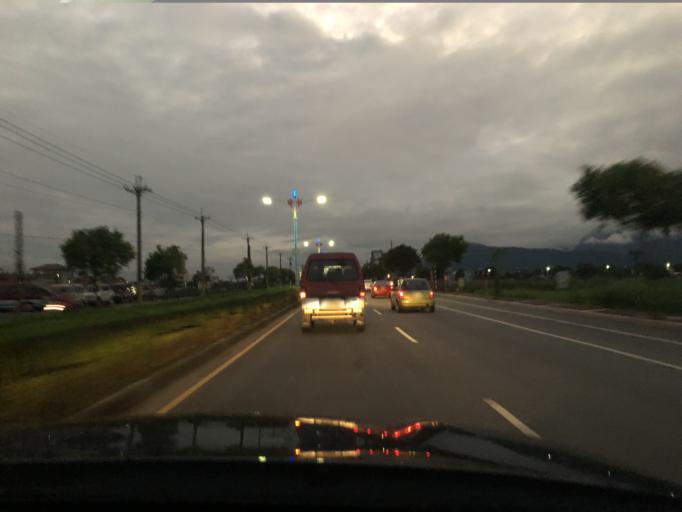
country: TW
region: Taiwan
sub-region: Hualien
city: Hualian
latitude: 23.9679
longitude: 121.5691
